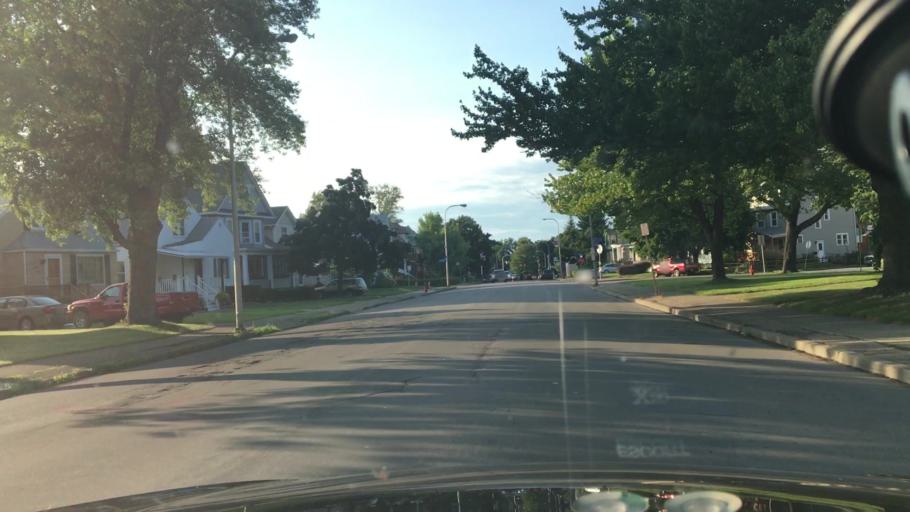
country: US
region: New York
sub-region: Erie County
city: West Seneca
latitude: 42.8436
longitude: -78.8092
